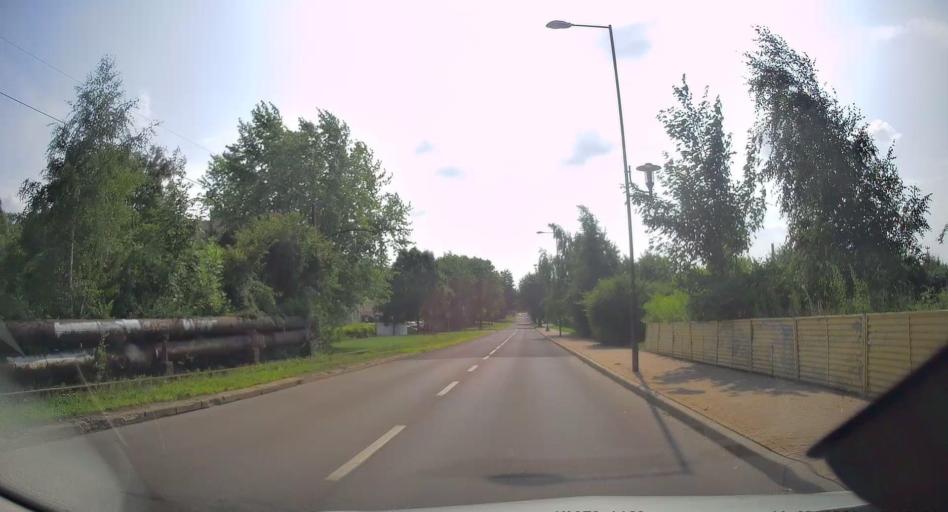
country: PL
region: Silesian Voivodeship
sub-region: Swietochlowice
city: Swietochlowice
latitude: 50.3189
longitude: 18.9225
